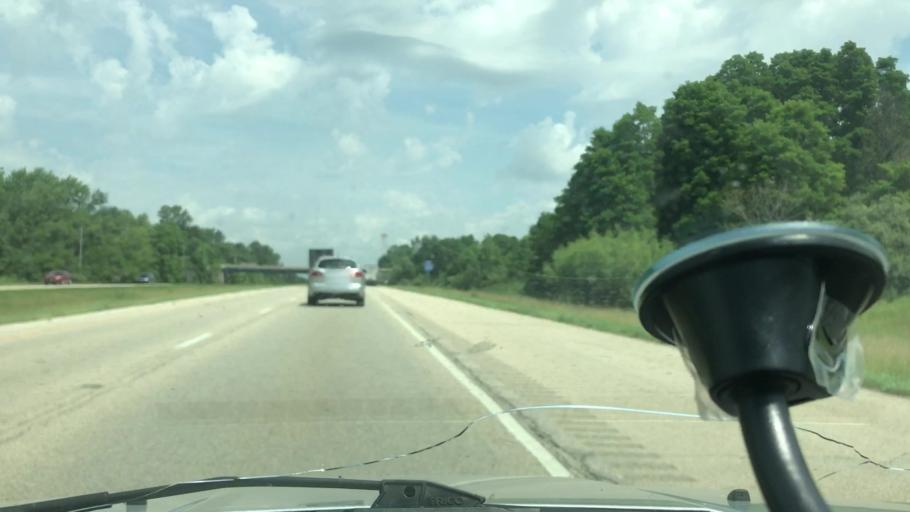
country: US
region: Illinois
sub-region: Peoria County
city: Bellevue
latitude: 40.6953
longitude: -89.6756
